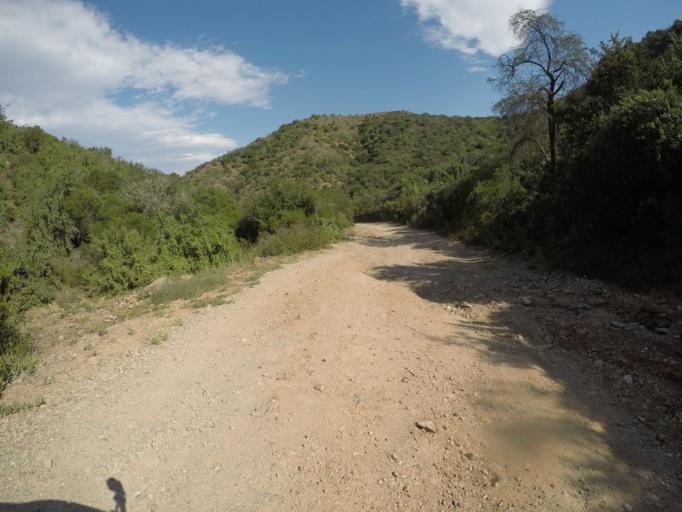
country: ZA
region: Eastern Cape
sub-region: Cacadu District Municipality
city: Kareedouw
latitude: -33.6552
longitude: 24.4022
